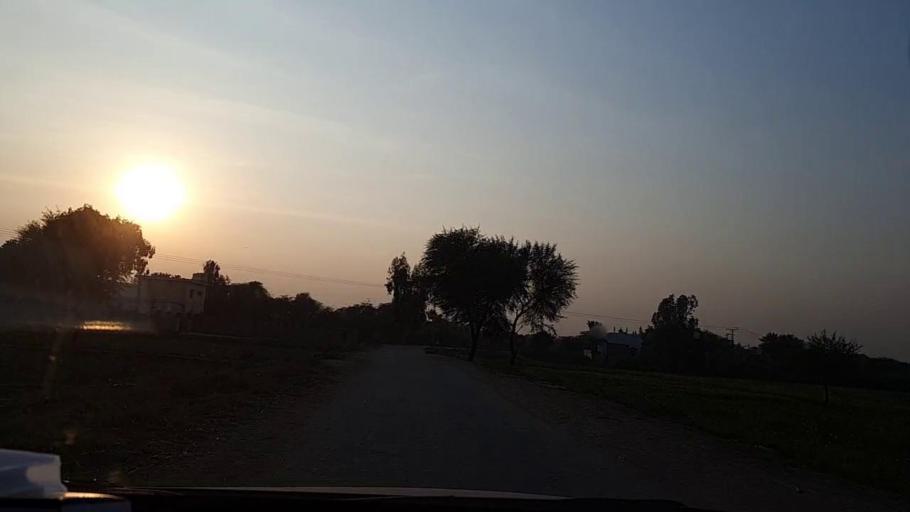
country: PK
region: Sindh
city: Tando Ghulam Ali
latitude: 25.1718
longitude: 68.9380
